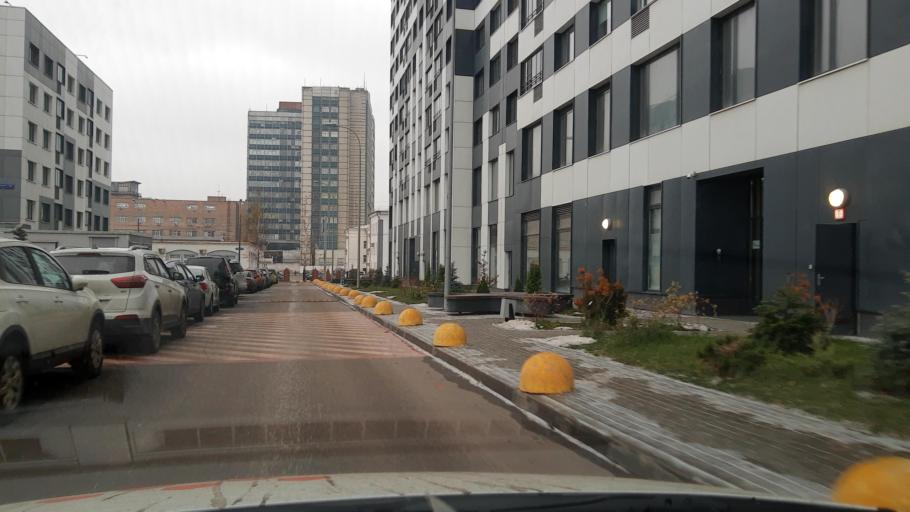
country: RU
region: Moscow
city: Ryazanskiy
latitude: 55.7595
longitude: 37.7389
